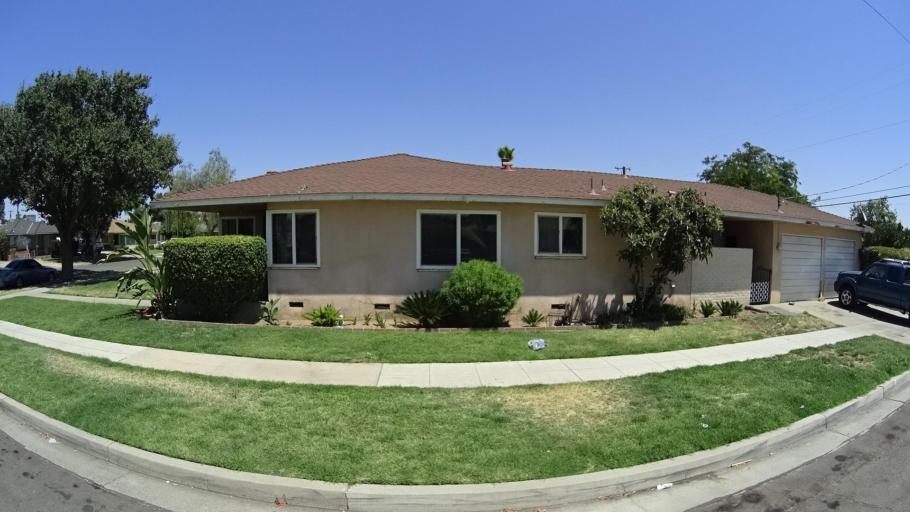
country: US
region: California
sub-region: Fresno County
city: Fresno
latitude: 36.7806
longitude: -119.7784
